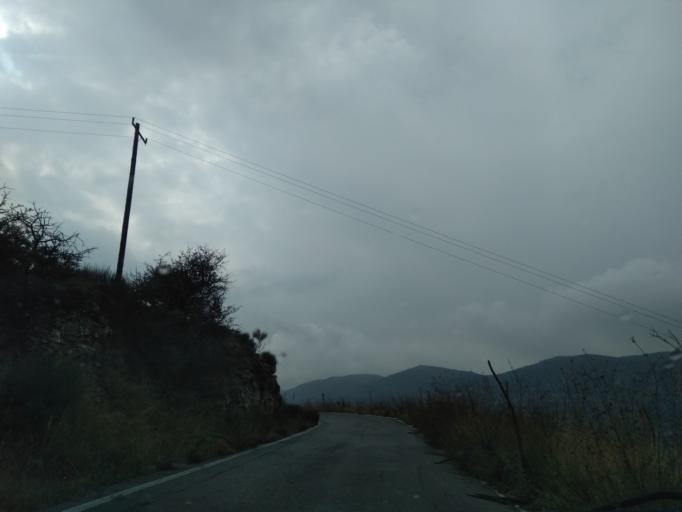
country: GR
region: Crete
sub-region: Nomos Lasithiou
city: Siteia
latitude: 35.1538
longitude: 26.0182
